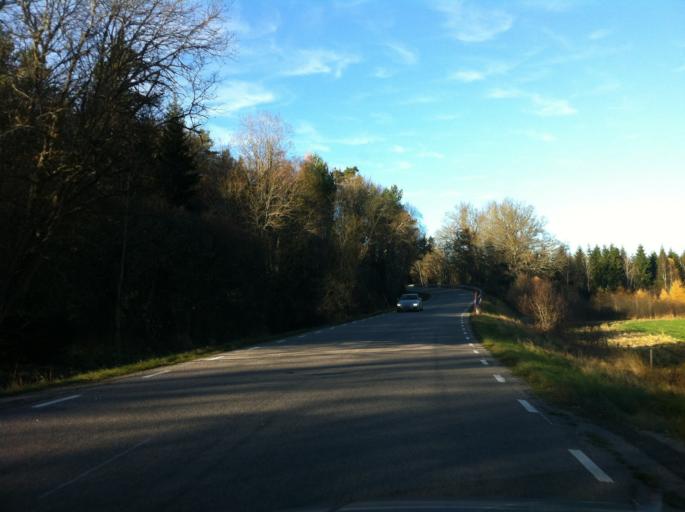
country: SE
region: Blekinge
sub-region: Ronneby Kommun
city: Brakne-Hoby
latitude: 56.1731
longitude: 15.1372
